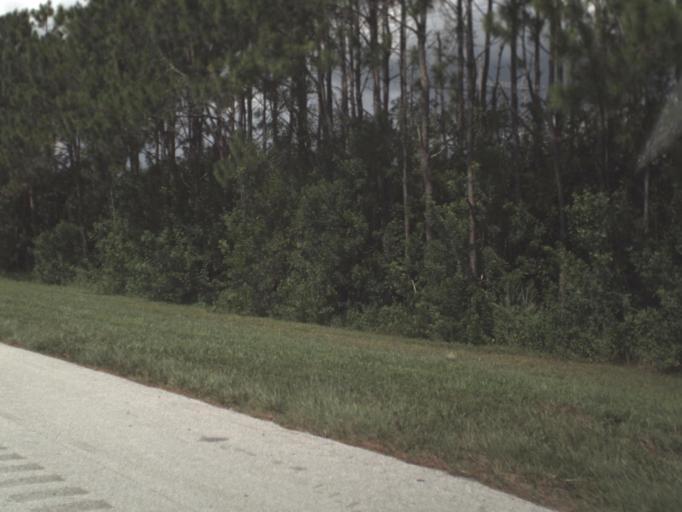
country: US
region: Florida
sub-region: Hillsborough County
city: Ruskin
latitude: 27.6634
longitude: -82.4344
